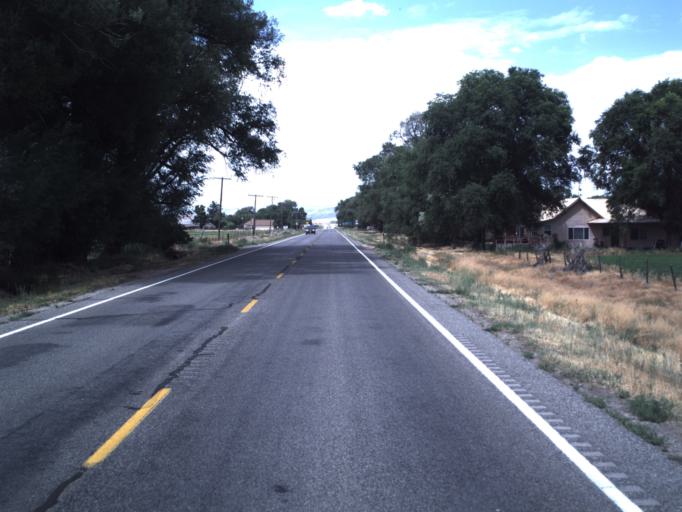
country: US
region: Utah
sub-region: Sanpete County
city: Moroni
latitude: 39.4718
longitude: -111.5628
